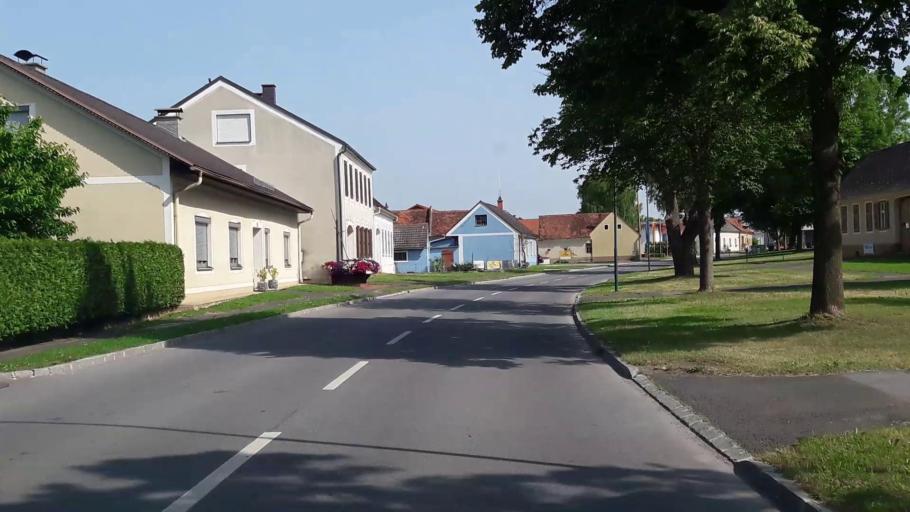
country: AT
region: Burgenland
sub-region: Politischer Bezirk Jennersdorf
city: Deutsch Kaltenbrunn
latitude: 47.0861
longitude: 16.1063
